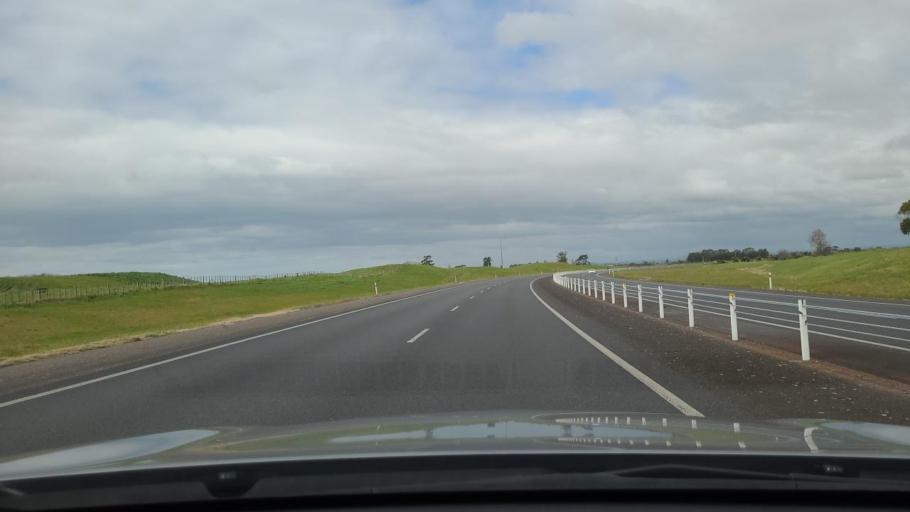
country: NZ
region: Bay of Plenty
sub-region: Western Bay of Plenty District
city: Maketu
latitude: -37.7328
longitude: 176.3445
